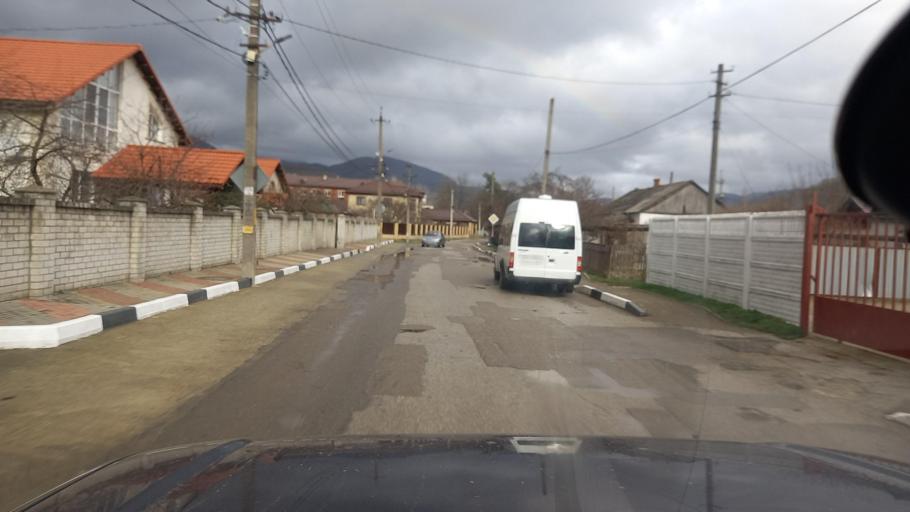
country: RU
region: Krasnodarskiy
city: Pshada
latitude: 44.4735
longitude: 38.3977
